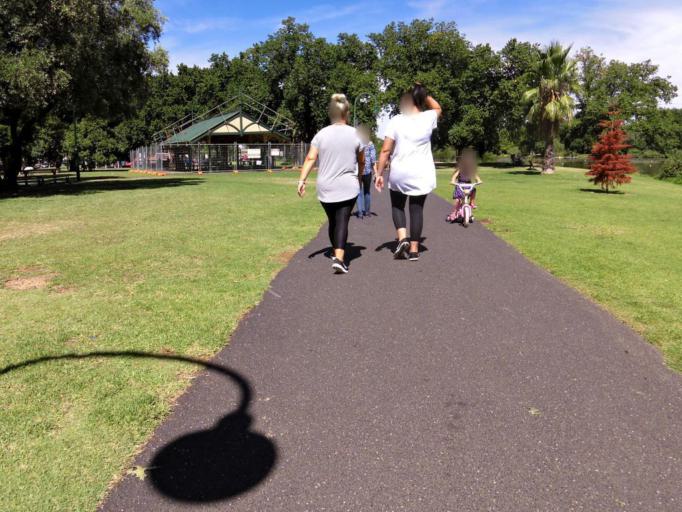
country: AU
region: Victoria
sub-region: Greater Bendigo
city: Bendigo
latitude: -36.7461
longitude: 144.2931
